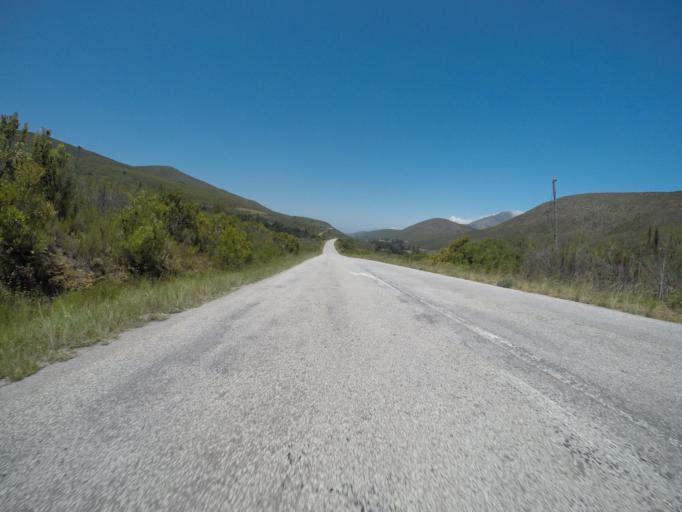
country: ZA
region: Eastern Cape
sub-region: Cacadu District Municipality
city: Kareedouw
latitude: -33.8617
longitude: 23.9997
